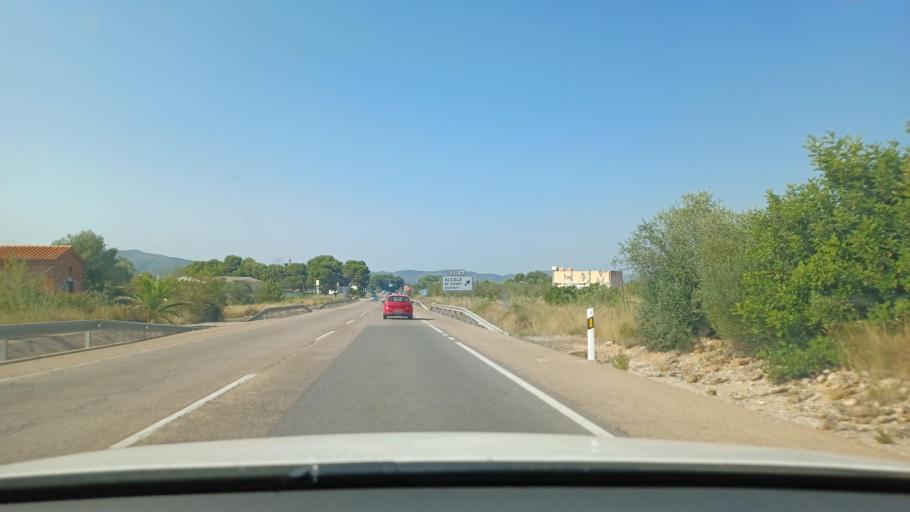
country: ES
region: Valencia
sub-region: Provincia de Castello
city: Alcala de Xivert
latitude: 40.2921
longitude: 0.2259
